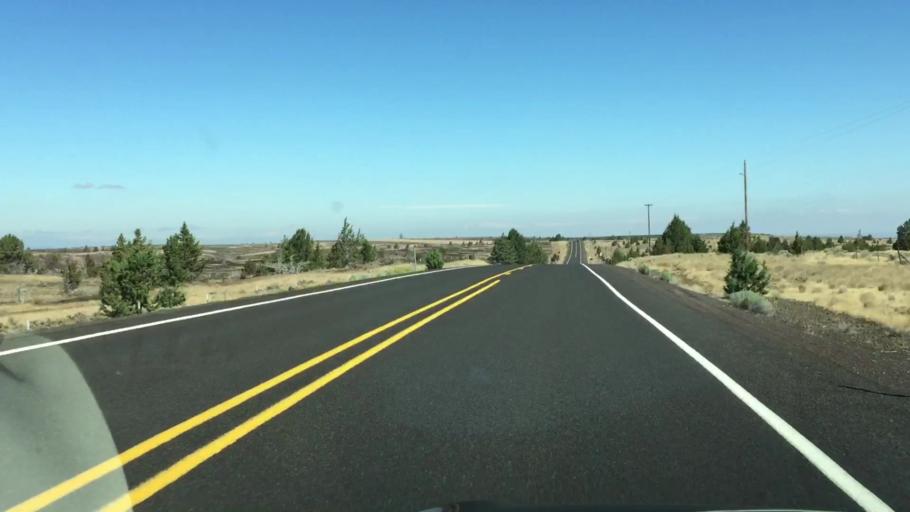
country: US
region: Oregon
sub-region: Jefferson County
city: Warm Springs
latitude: 45.0223
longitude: -120.9916
